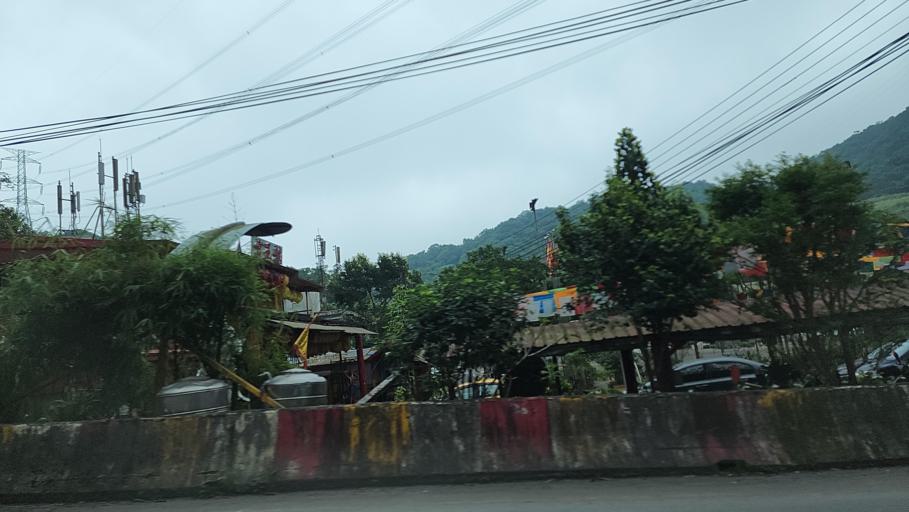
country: TW
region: Taiwan
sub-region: Keelung
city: Keelung
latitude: 25.1652
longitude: 121.6859
